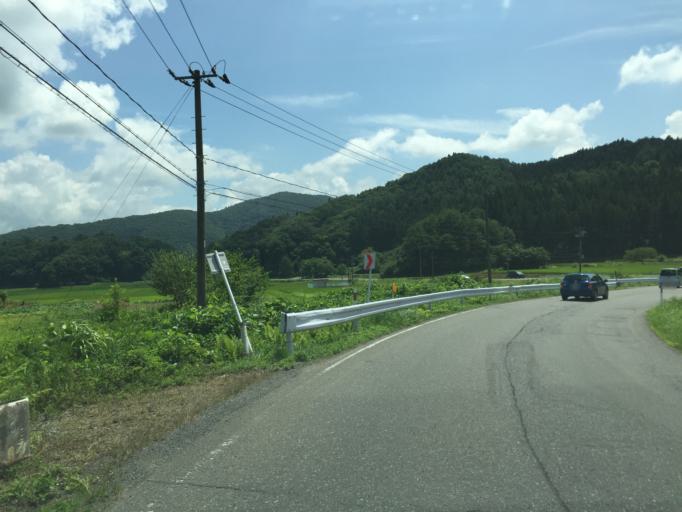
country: JP
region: Fukushima
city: Inawashiro
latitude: 37.4088
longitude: 140.0614
